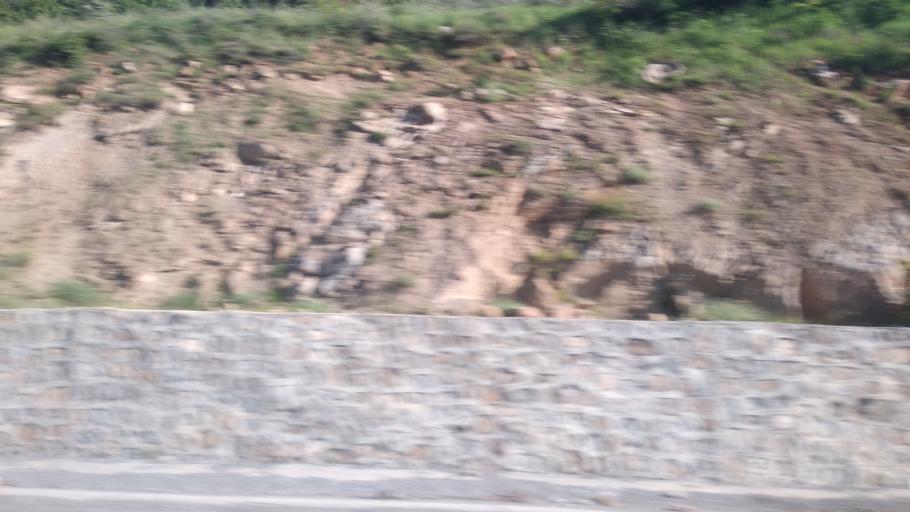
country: TR
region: Bitlis
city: Resadiye
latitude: 38.4761
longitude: 42.5310
